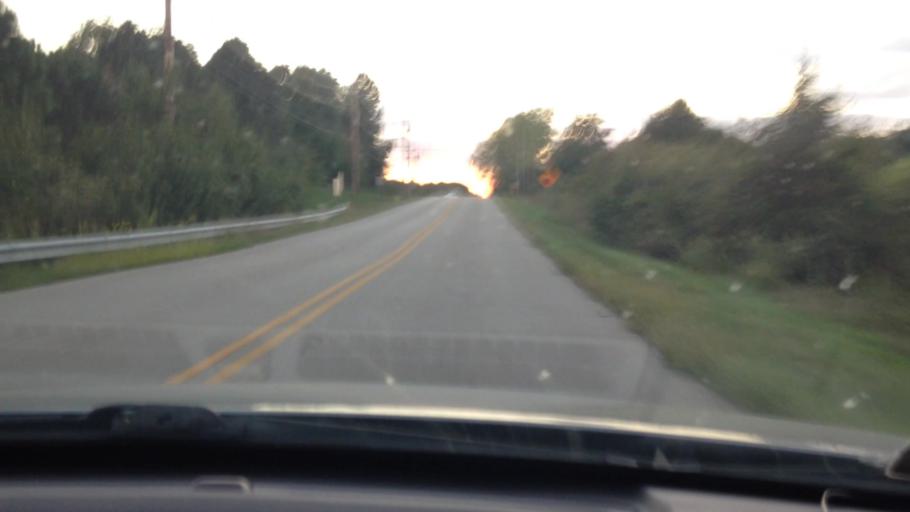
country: US
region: Kansas
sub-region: Leavenworth County
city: Lansing
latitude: 39.1867
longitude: -94.8620
